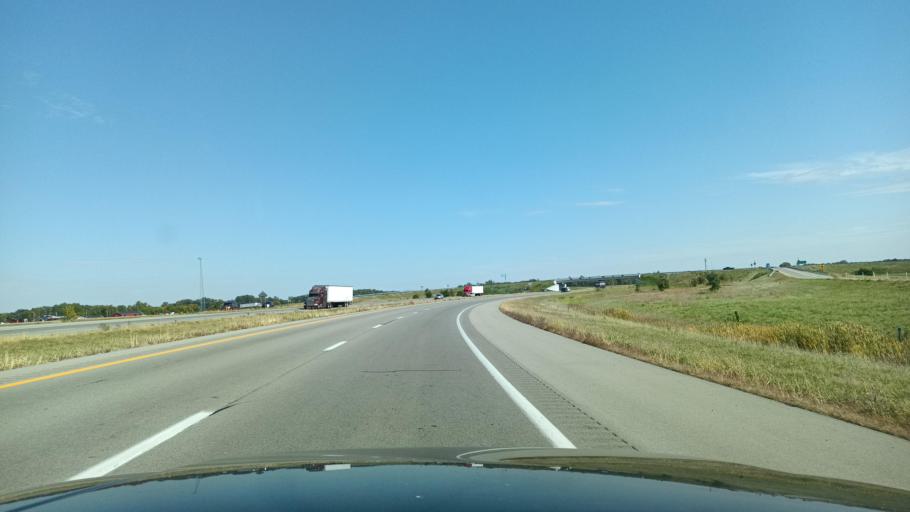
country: US
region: Ohio
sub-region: Henry County
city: Liberty Center
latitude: 41.4289
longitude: -84.0144
